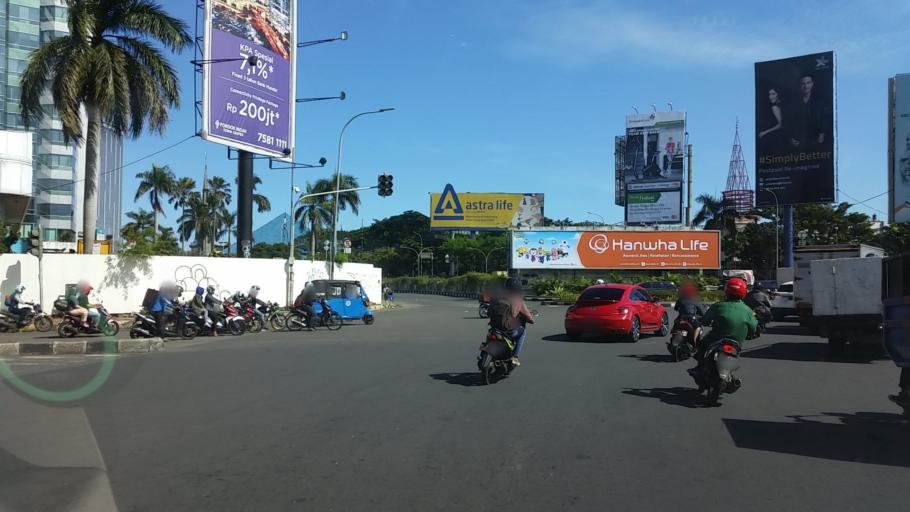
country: ID
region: Banten
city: South Tangerang
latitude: -6.2640
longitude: 106.7834
